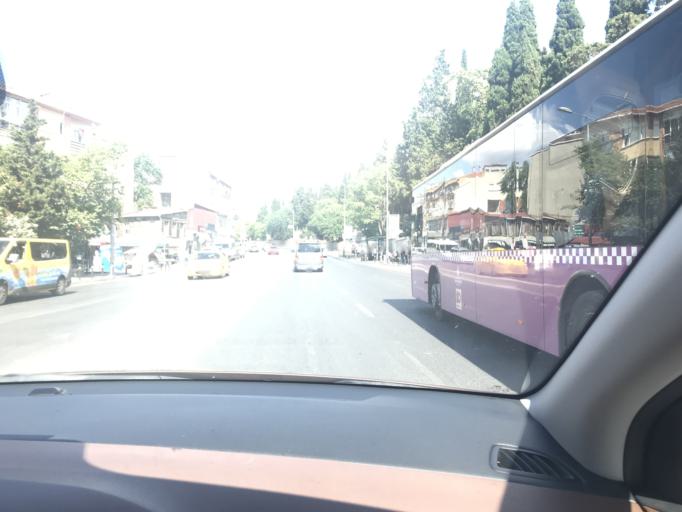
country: TR
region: Istanbul
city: UEskuedar
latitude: 41.0131
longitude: 29.0205
